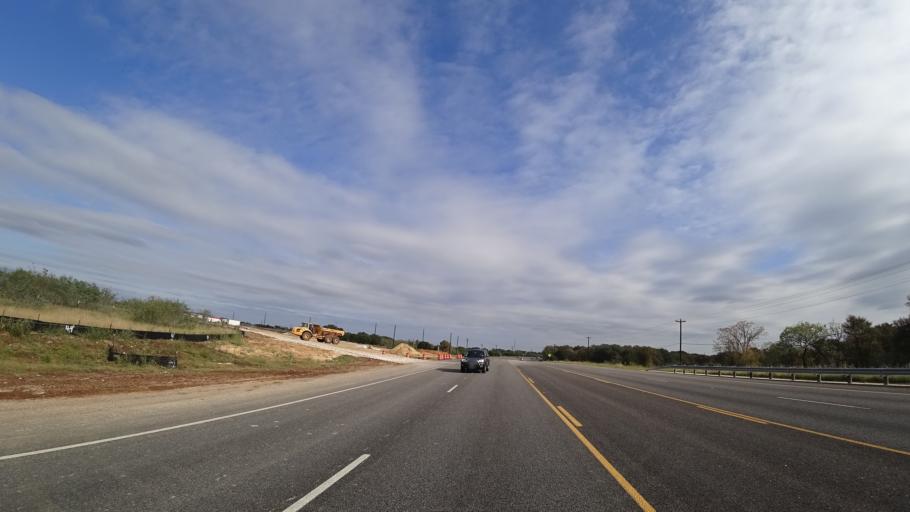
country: US
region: Texas
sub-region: Travis County
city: Manchaca
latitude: 30.1286
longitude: -97.8590
